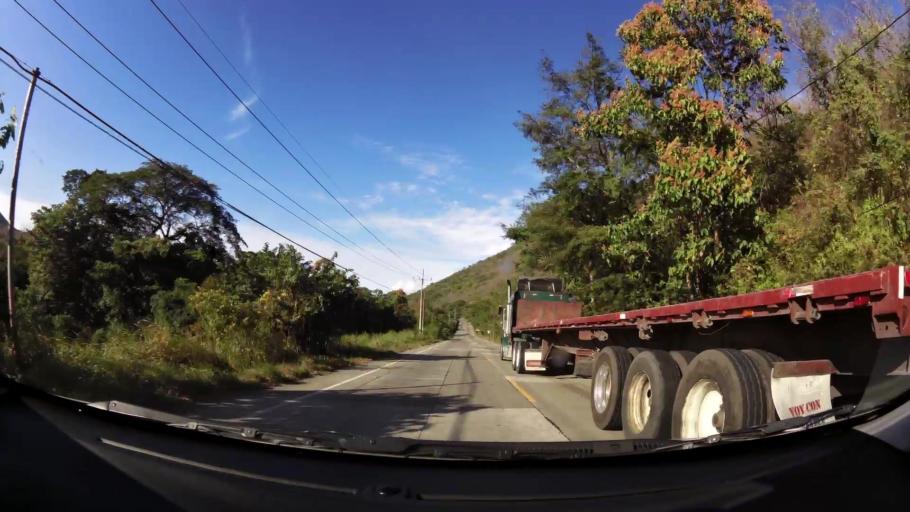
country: SV
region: Santa Ana
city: Metapan
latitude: 14.2590
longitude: -89.4606
